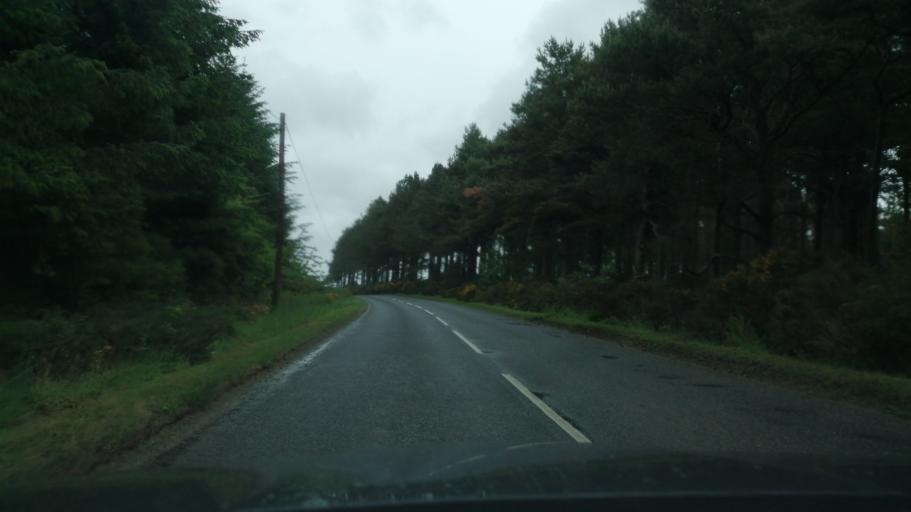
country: GB
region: Scotland
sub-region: Aberdeenshire
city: Portsoy
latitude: 57.6413
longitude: -2.7129
